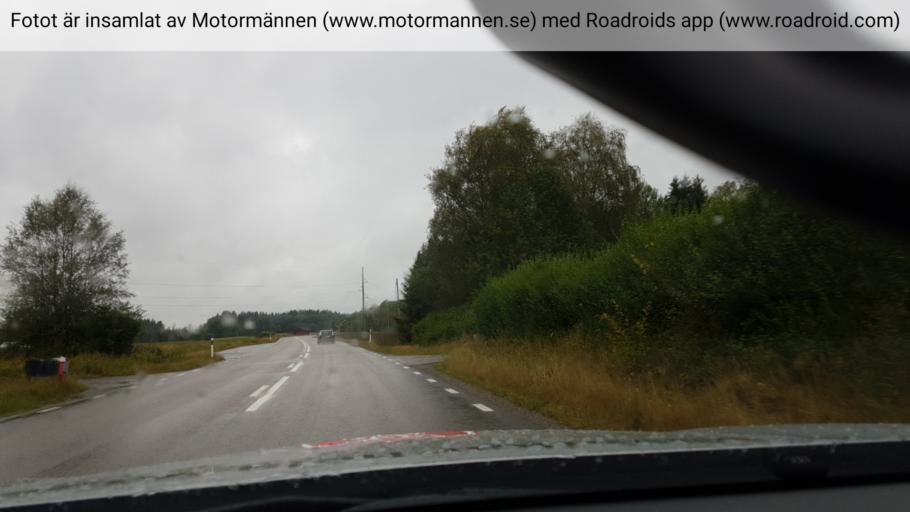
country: SE
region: Vaestra Goetaland
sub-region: Dals-Ed Kommun
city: Ed
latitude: 58.8902
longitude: 11.9188
